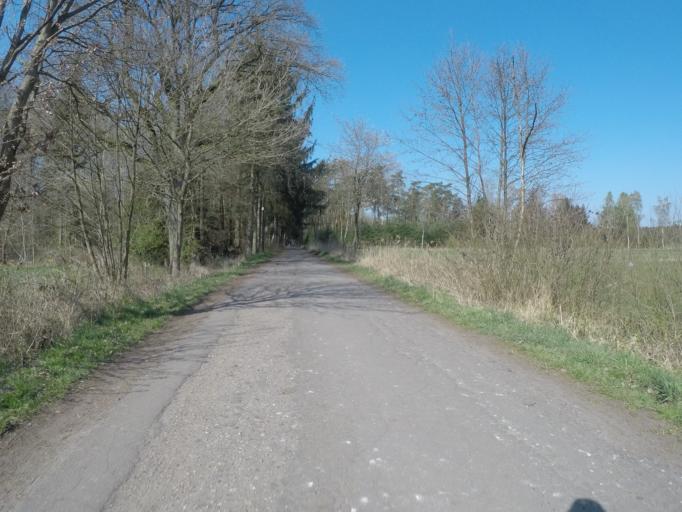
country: DE
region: Schleswig-Holstein
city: Rellingen
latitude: 53.6175
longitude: 9.7799
